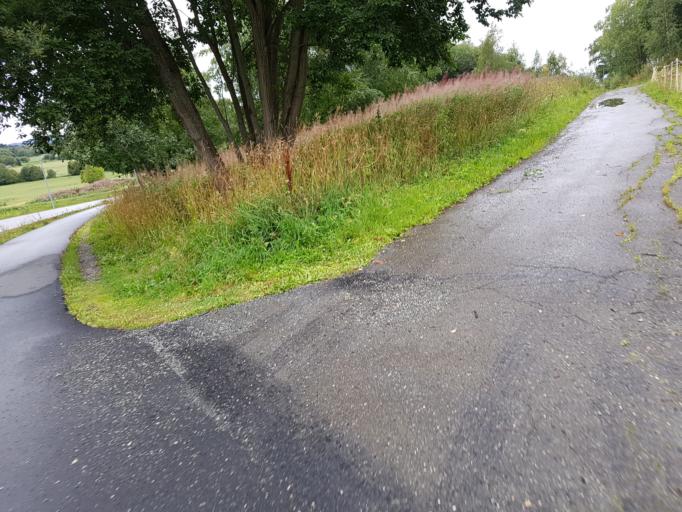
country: NO
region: Sor-Trondelag
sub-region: Trondheim
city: Trondheim
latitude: 63.4042
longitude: 10.4817
